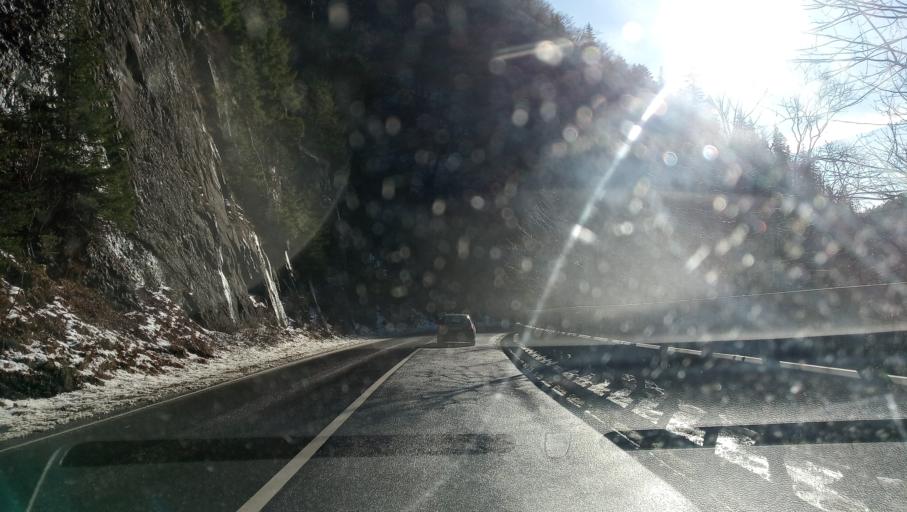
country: RO
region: Brasov
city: Crivina
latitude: 45.4748
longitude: 25.9207
